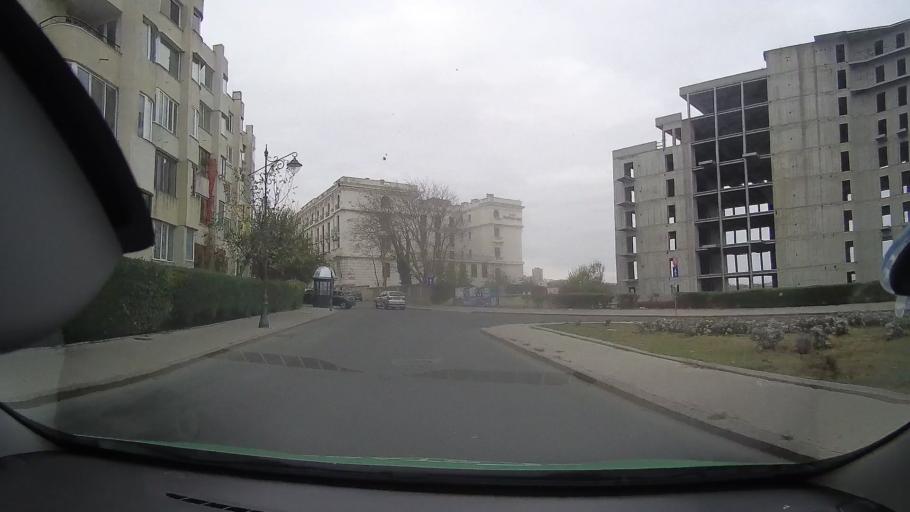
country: RO
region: Constanta
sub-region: Municipiul Constanta
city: Constanta
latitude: 44.1727
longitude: 28.6640
